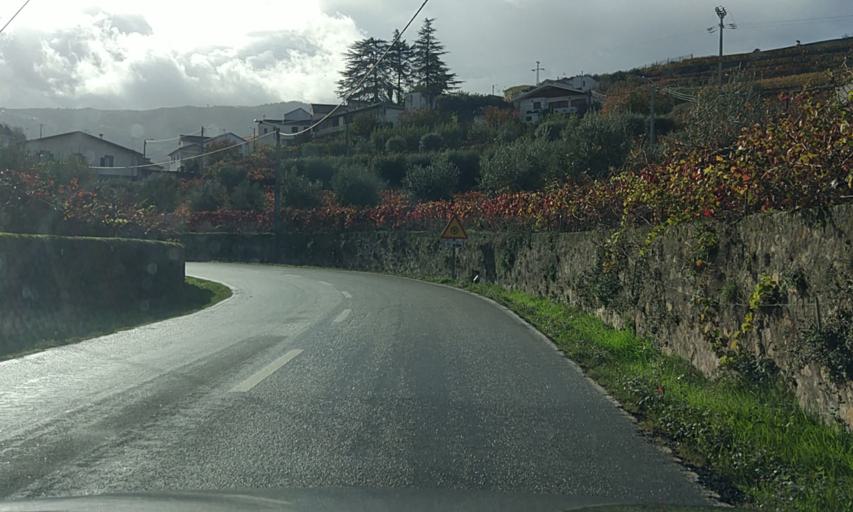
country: PT
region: Vila Real
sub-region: Peso da Regua
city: Peso da Regua
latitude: 41.1302
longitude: -7.7956
